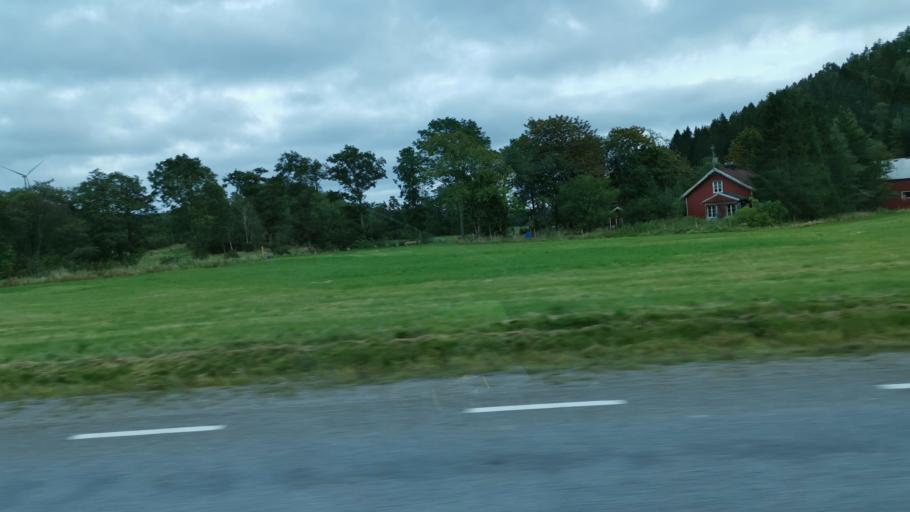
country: SE
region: Vaestra Goetaland
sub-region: Lysekils Kommun
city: Brastad
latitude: 58.5611
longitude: 11.4716
